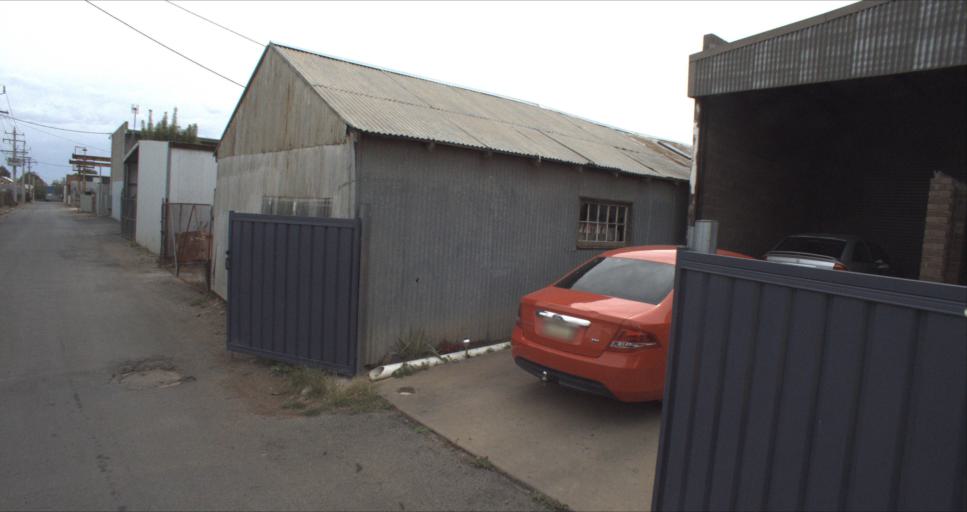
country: AU
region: New South Wales
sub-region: Leeton
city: Leeton
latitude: -34.5536
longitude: 146.3999
